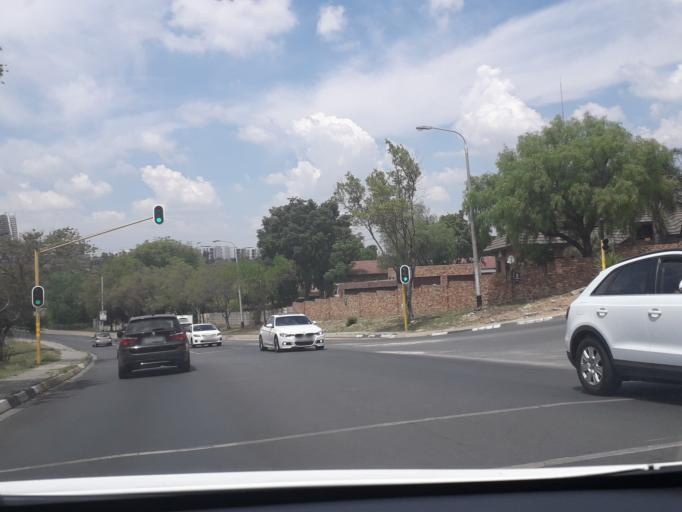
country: ZA
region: Gauteng
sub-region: City of Johannesburg Metropolitan Municipality
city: Midrand
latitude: -26.0035
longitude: 28.1036
